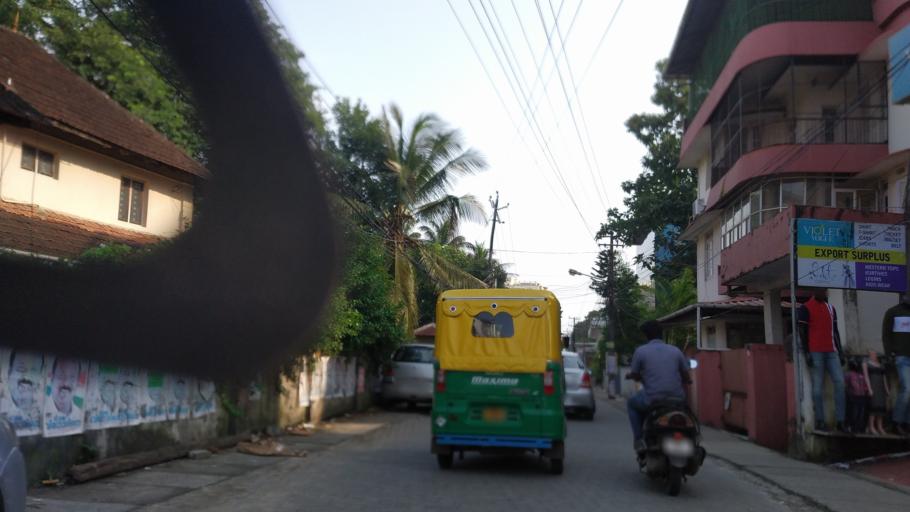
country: IN
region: Kerala
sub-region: Ernakulam
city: Cochin
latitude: 9.9900
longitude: 76.2884
